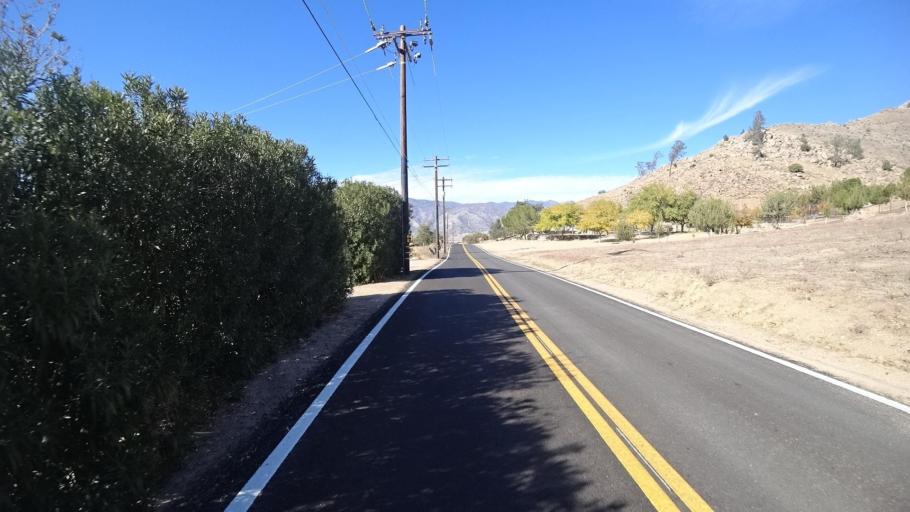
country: US
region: California
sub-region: Kern County
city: Lake Isabella
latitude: 35.5967
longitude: -118.4522
